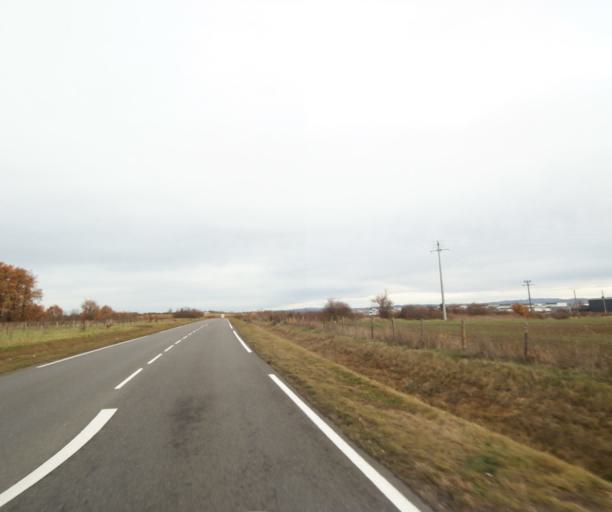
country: FR
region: Rhone-Alpes
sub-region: Departement de la Loire
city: Sury-le-Comtal
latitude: 45.5157
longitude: 4.1899
